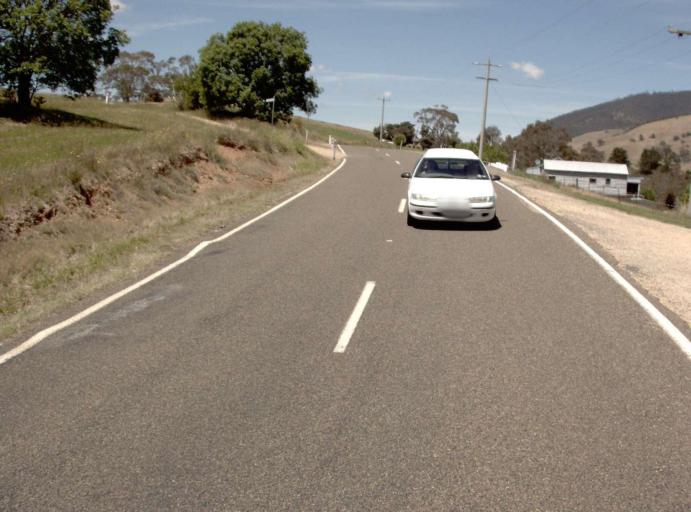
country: AU
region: Victoria
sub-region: Alpine
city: Mount Beauty
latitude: -37.1042
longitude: 147.5820
